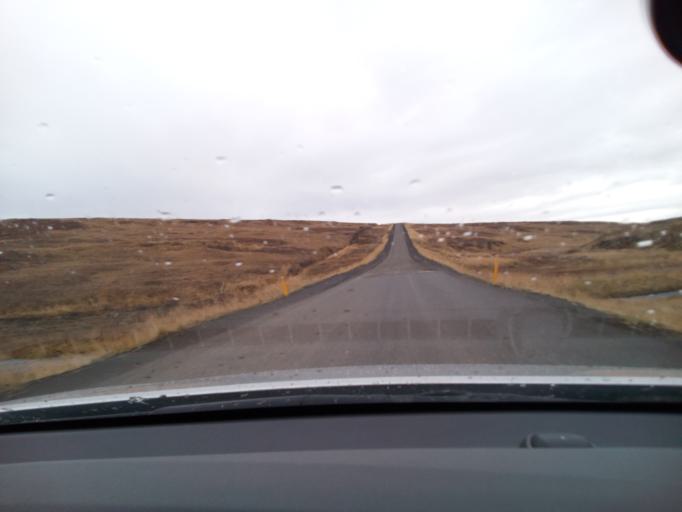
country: IS
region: Northeast
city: Laugar
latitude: 65.7922
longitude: -17.2337
